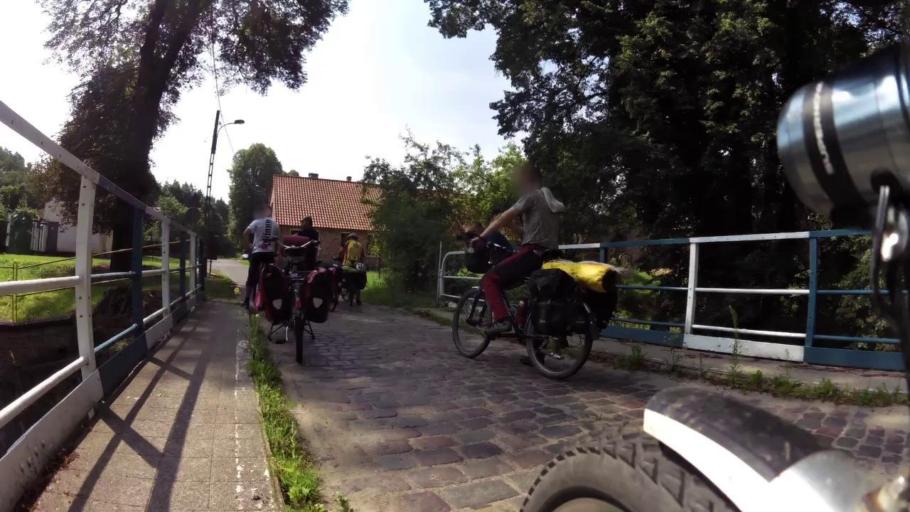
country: PL
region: West Pomeranian Voivodeship
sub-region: Powiat mysliborski
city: Boleszkowice
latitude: 52.6795
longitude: 14.5980
